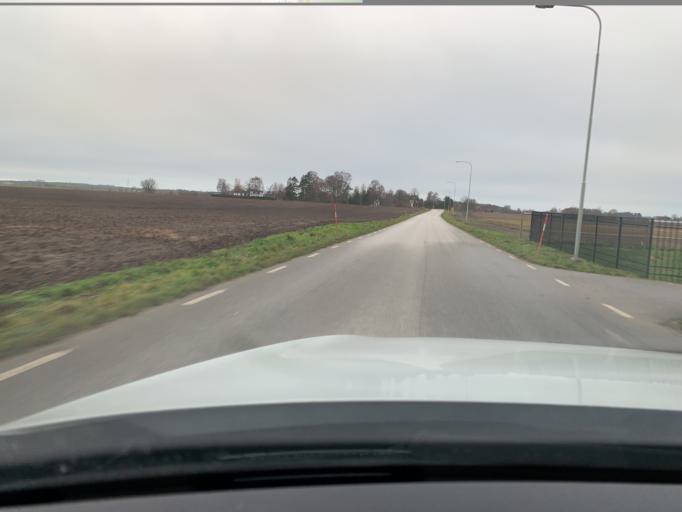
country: SE
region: Skane
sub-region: Kavlinge Kommun
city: Hofterup
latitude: 55.8378
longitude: 13.0124
